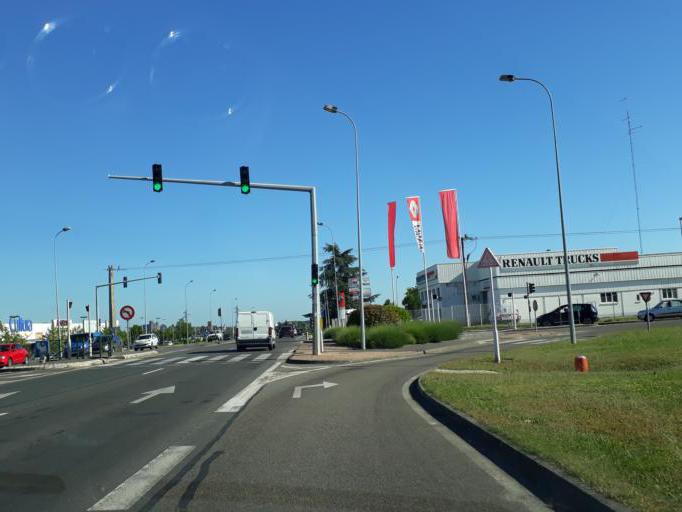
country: FR
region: Centre
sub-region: Departement du Cher
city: Saint-Doulchard
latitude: 47.1145
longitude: 2.3759
